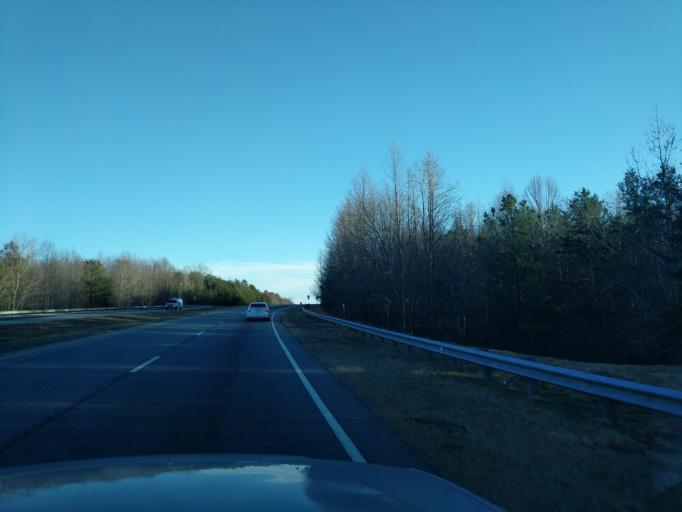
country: US
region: Georgia
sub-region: Stephens County
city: Toccoa
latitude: 34.5906
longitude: -83.4164
